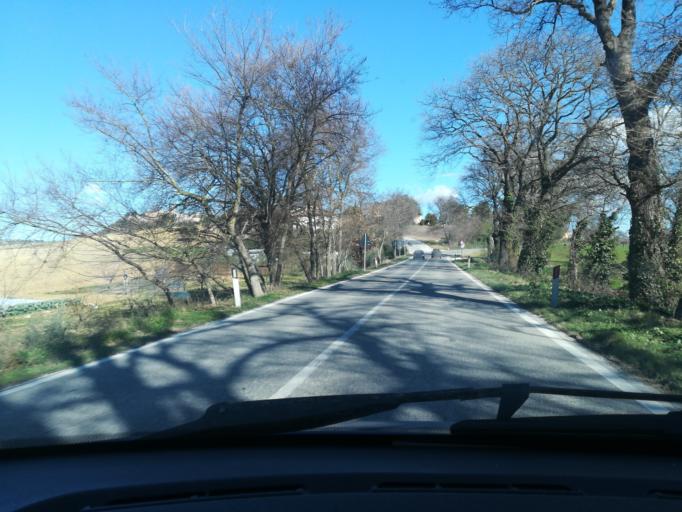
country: IT
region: The Marches
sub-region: Provincia di Macerata
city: Montecassiano
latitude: 43.3524
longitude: 13.4372
